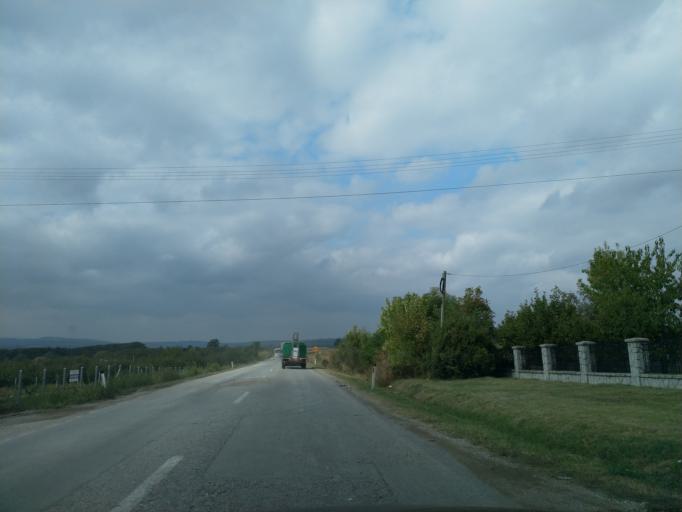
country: RS
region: Central Serbia
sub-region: Sumadijski Okrug
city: Kragujevac
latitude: 44.1017
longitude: 20.8547
